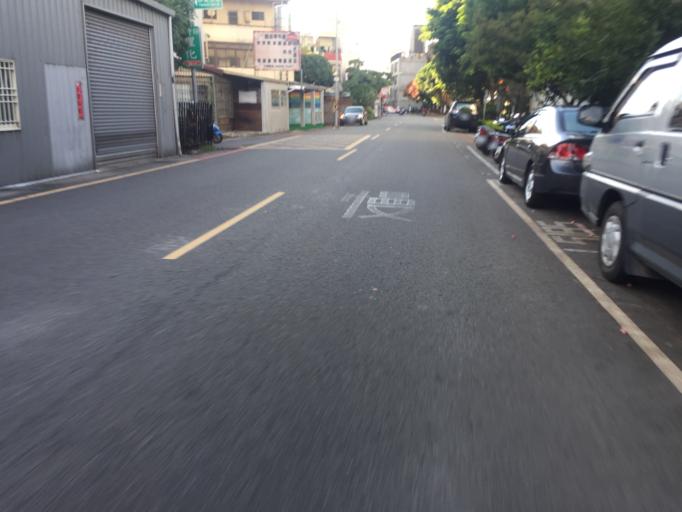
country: TW
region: Taiwan
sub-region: Hsinchu
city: Hsinchu
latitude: 24.8180
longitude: 120.9773
